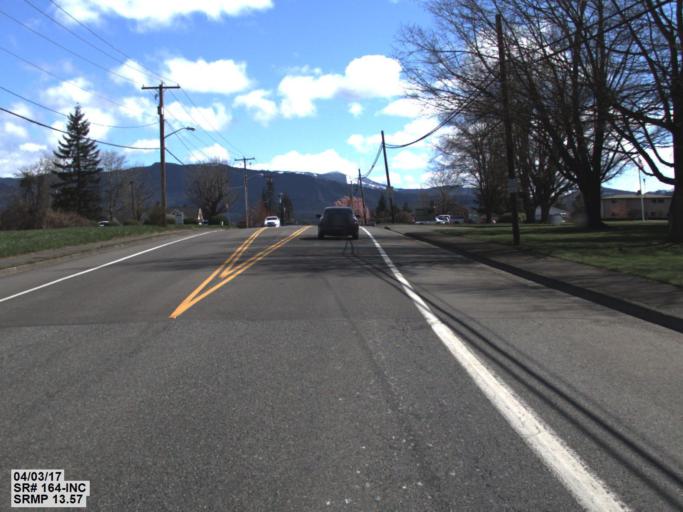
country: US
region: Washington
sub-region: King County
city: Enumclaw
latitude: 47.2066
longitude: -122.0107
